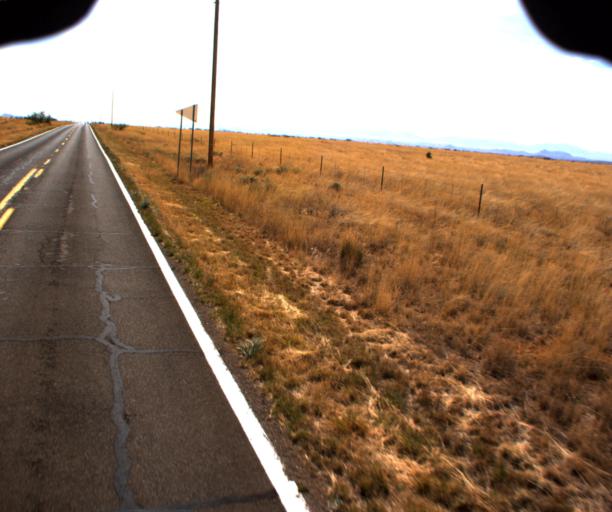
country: US
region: Arizona
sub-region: Cochise County
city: Willcox
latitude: 31.9894
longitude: -109.4518
